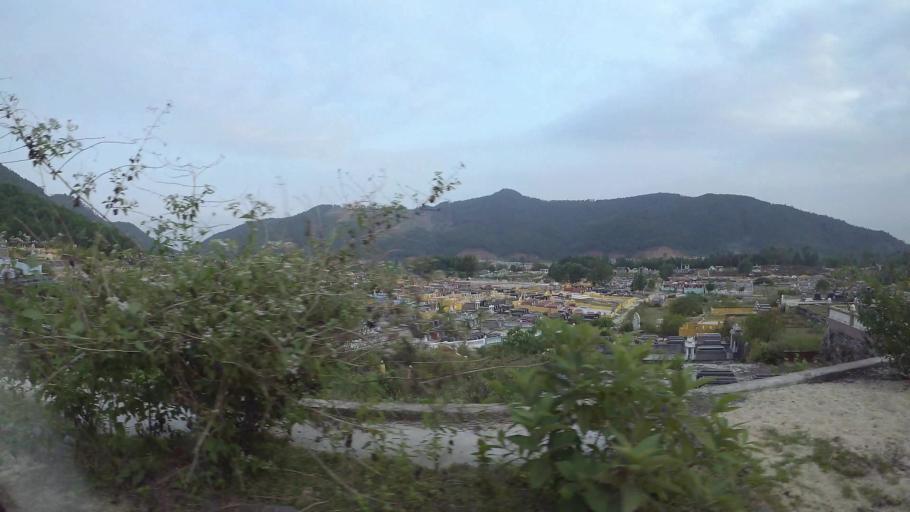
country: VN
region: Da Nang
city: Lien Chieu
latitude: 16.0625
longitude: 108.1184
